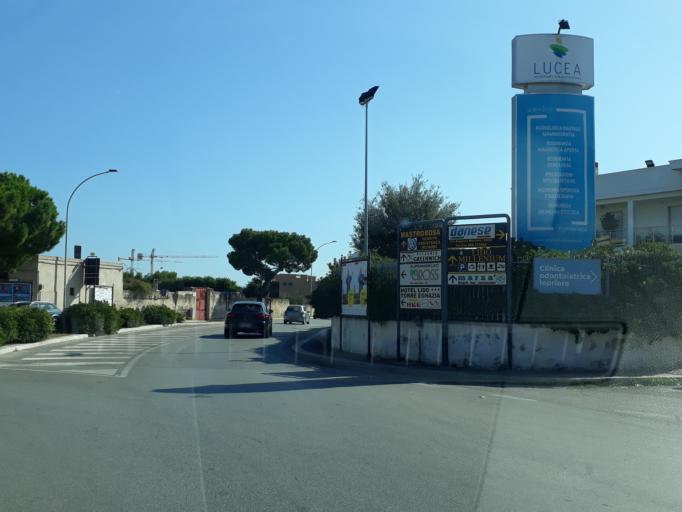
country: IT
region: Apulia
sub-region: Provincia di Bari
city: Monopoli
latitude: 40.9427
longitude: 17.3035
